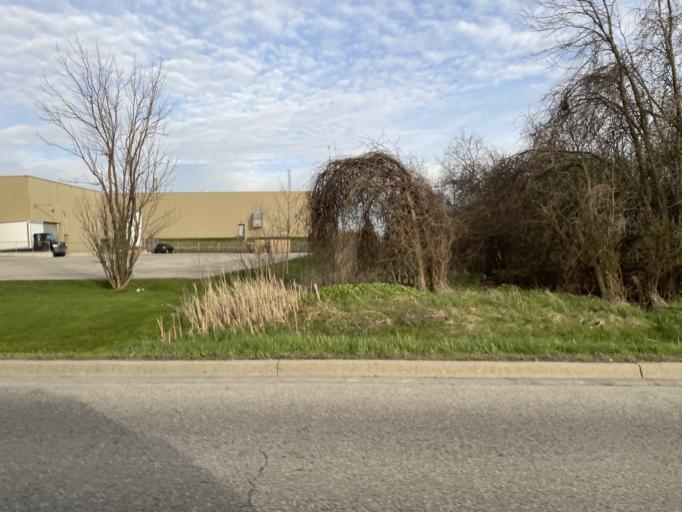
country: CA
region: Ontario
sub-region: Wellington County
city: Guelph
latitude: 43.5331
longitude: -80.3214
